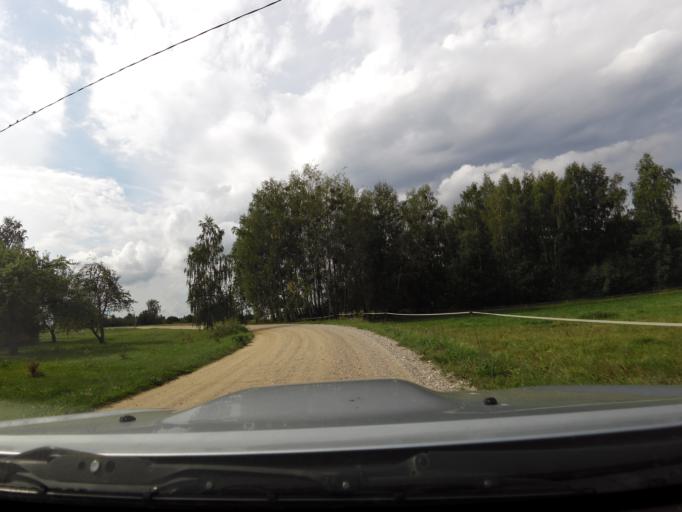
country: LT
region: Vilnius County
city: Elektrenai
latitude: 54.9187
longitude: 24.7342
